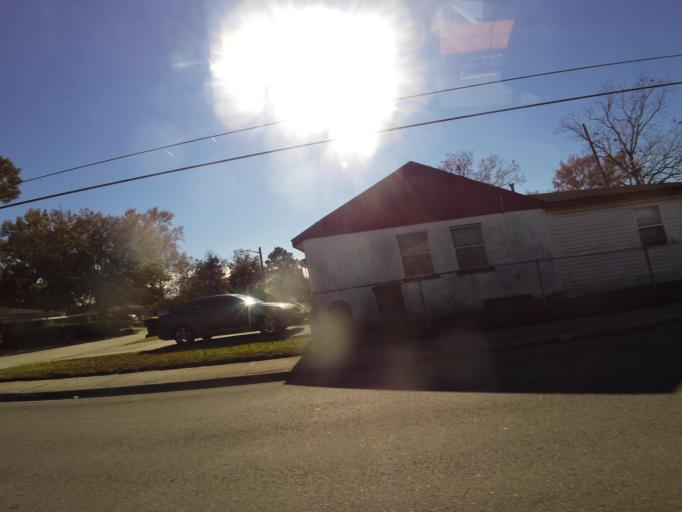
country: US
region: Georgia
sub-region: Chatham County
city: Savannah
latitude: 32.0743
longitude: -81.1230
